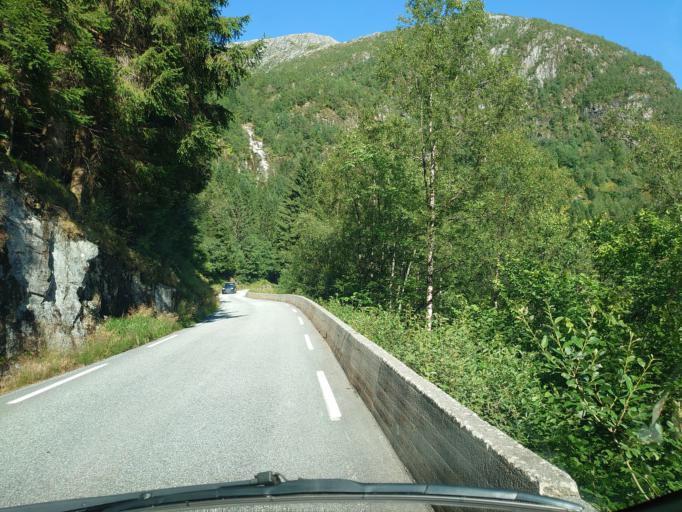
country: NO
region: Hordaland
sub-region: Vaksdal
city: Dale
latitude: 60.5877
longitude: 5.8497
